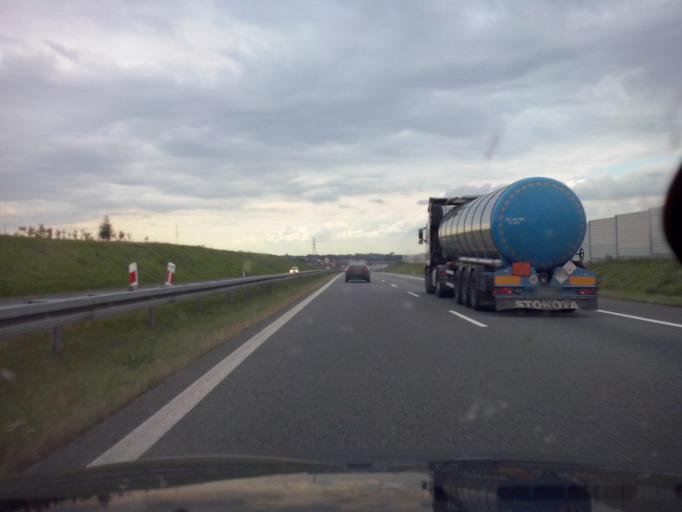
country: PL
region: Lesser Poland Voivodeship
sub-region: Powiat wielicki
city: Podleze
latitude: 50.0006
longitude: 20.1901
